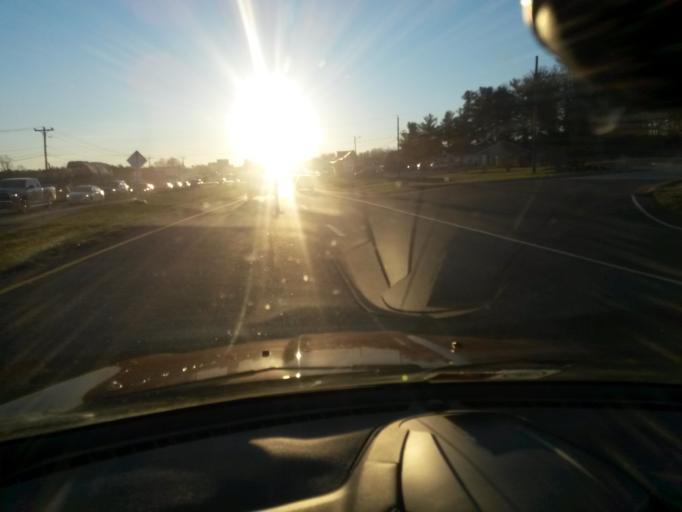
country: US
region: Virginia
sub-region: Franklin County
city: Rocky Mount
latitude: 37.0710
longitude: -79.8965
